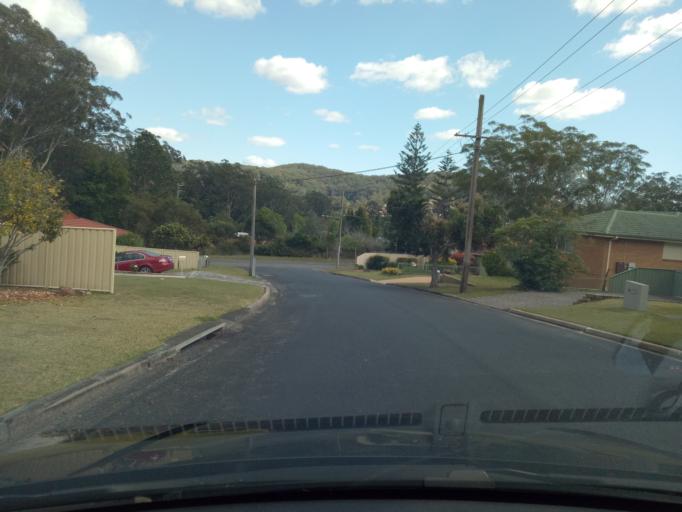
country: AU
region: New South Wales
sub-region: Gosford Shire
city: Narara
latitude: -33.3920
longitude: 151.3540
